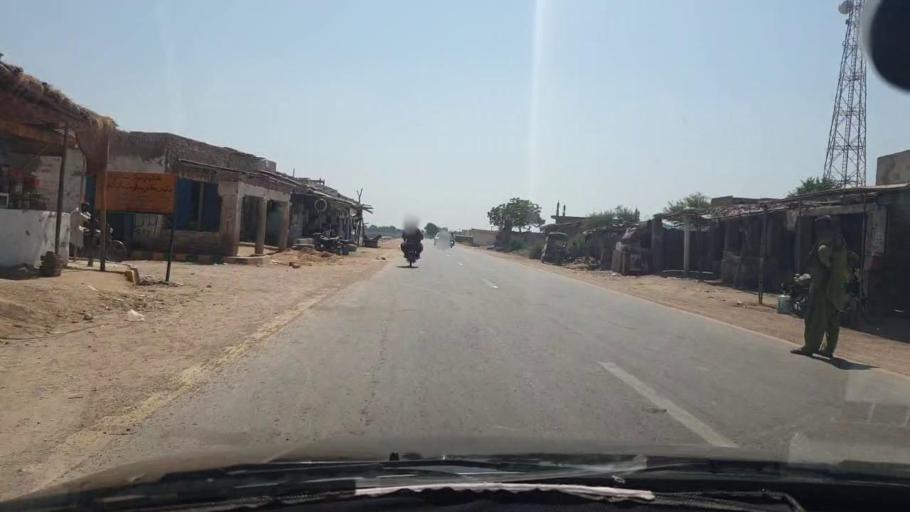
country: PK
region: Sindh
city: Chambar
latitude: 25.3323
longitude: 68.7977
